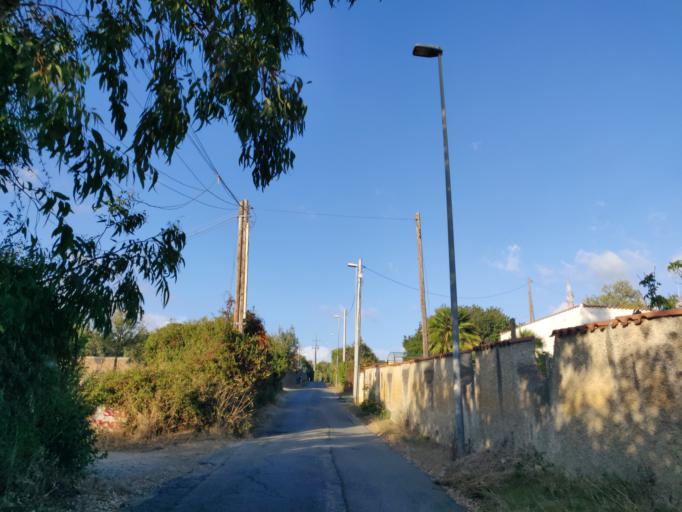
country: IT
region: Latium
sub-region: Citta metropolitana di Roma Capitale
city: Civitavecchia
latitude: 42.0911
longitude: 11.8147
